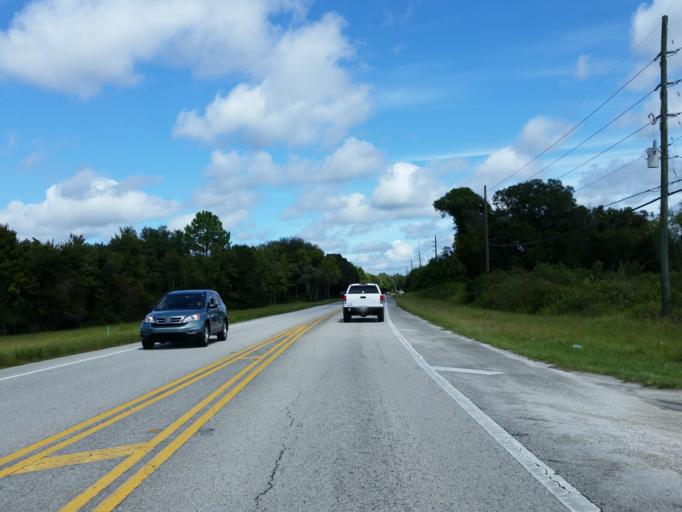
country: US
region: Florida
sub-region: Pasco County
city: Land O' Lakes
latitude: 28.1962
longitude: -82.3993
